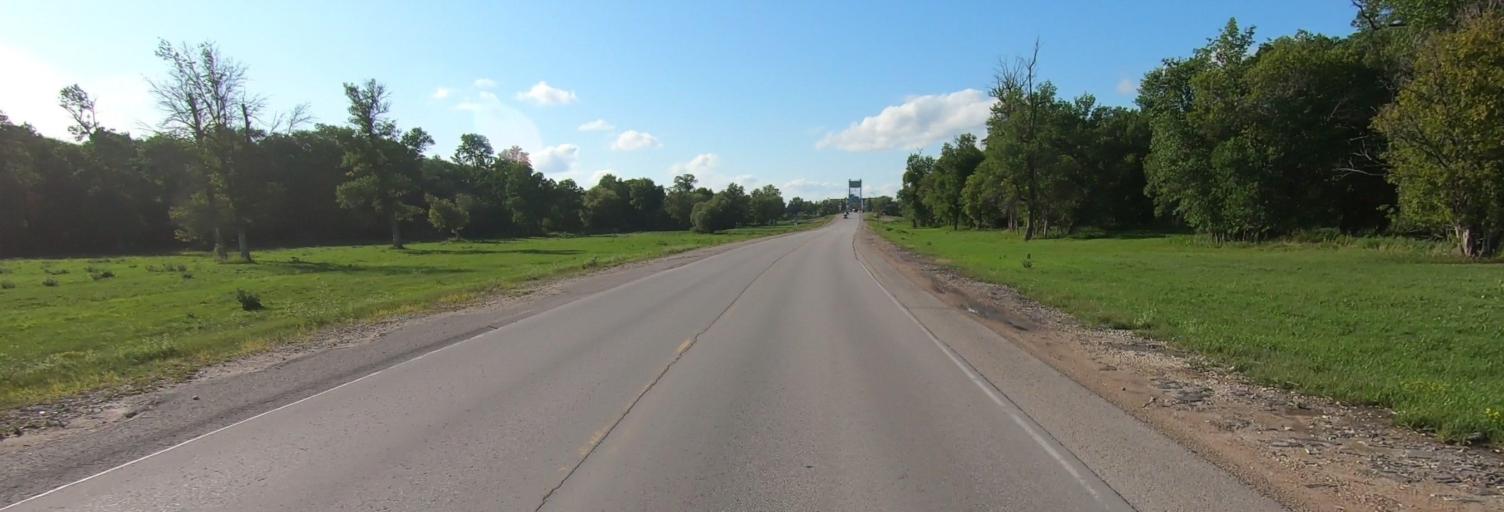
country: CA
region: Manitoba
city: Selkirk
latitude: 50.1380
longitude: -96.8640
